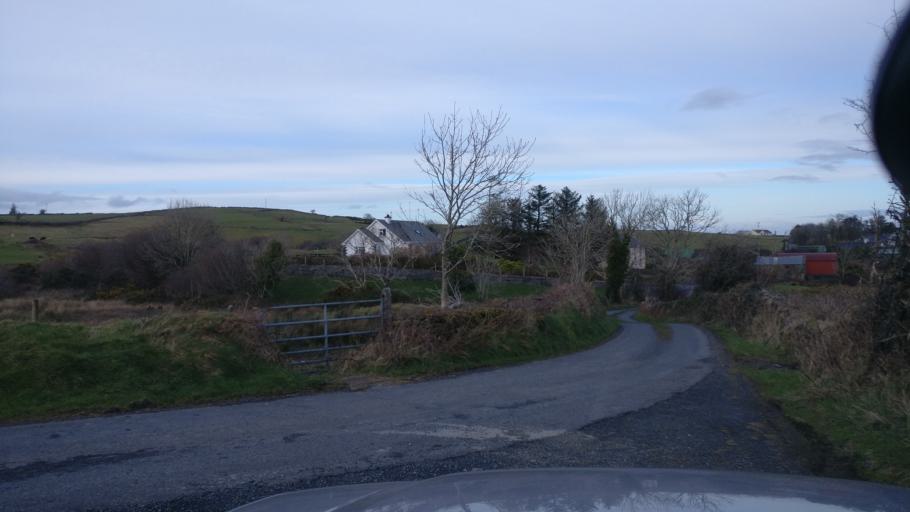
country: IE
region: Connaught
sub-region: County Galway
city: Oughterard
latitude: 53.5266
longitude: -9.3756
